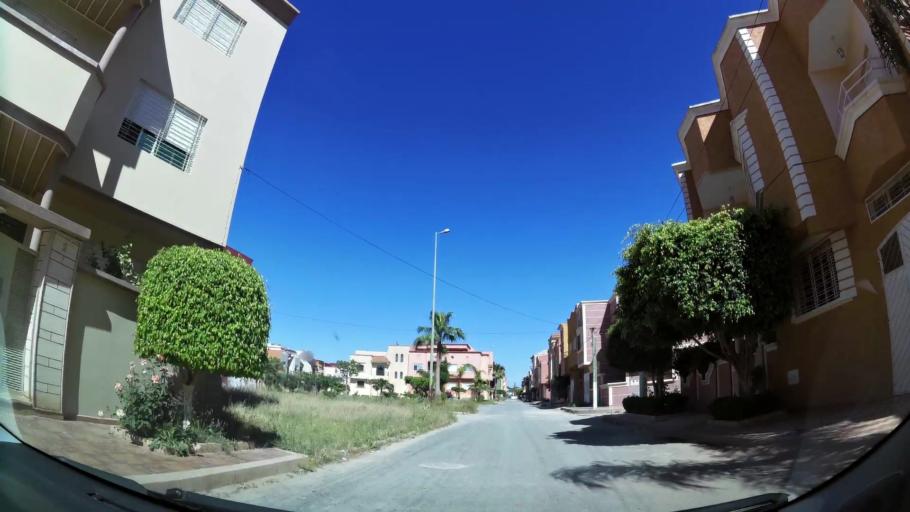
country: MA
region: Oriental
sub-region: Berkane-Taourirt
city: Berkane
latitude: 34.9405
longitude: -2.3298
